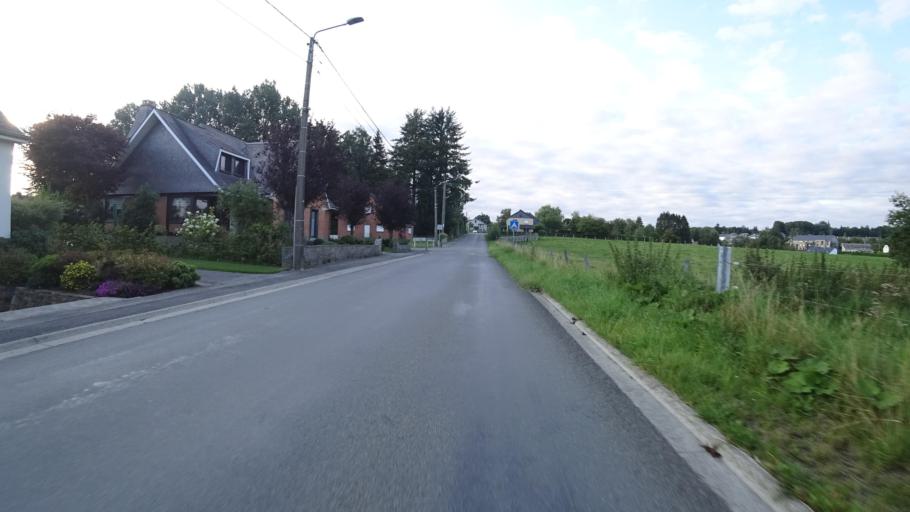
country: BE
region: Wallonia
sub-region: Province du Luxembourg
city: Neufchateau
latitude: 49.9112
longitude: 5.3839
